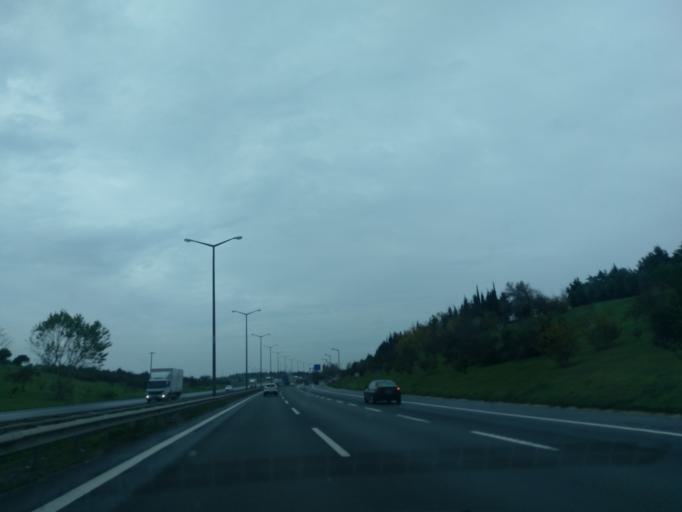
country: TR
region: Istanbul
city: Silivri
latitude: 41.1082
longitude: 28.2718
